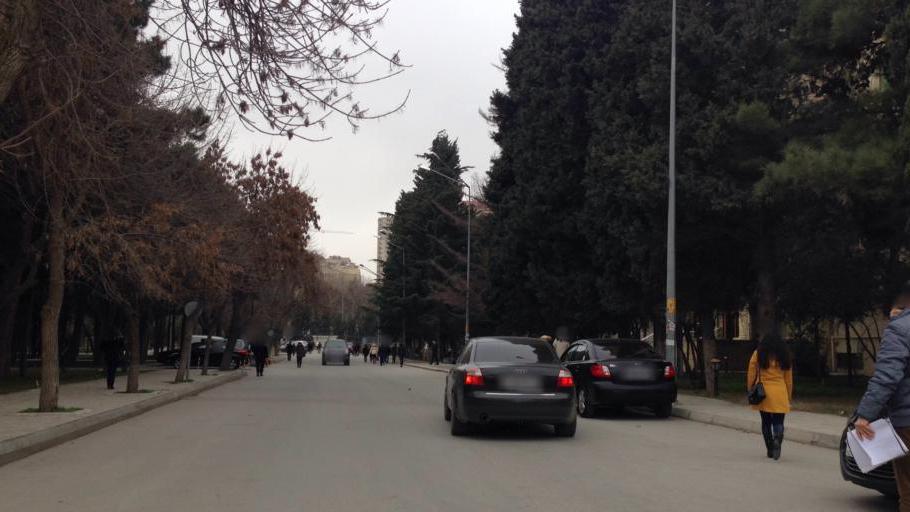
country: AZ
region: Baki
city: Badamdar
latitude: 40.3740
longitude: 49.8146
